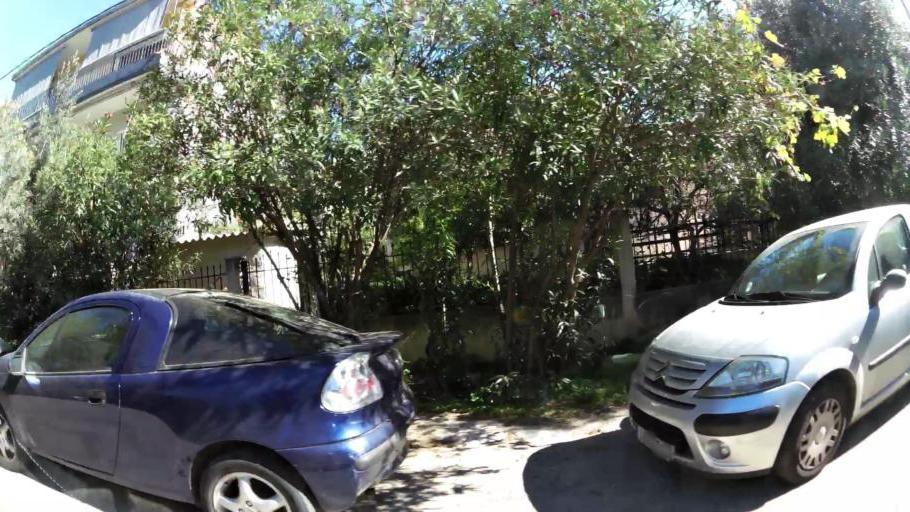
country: GR
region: Attica
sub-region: Nomarchia Athinas
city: Khalandrion
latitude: 38.0290
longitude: 23.8132
